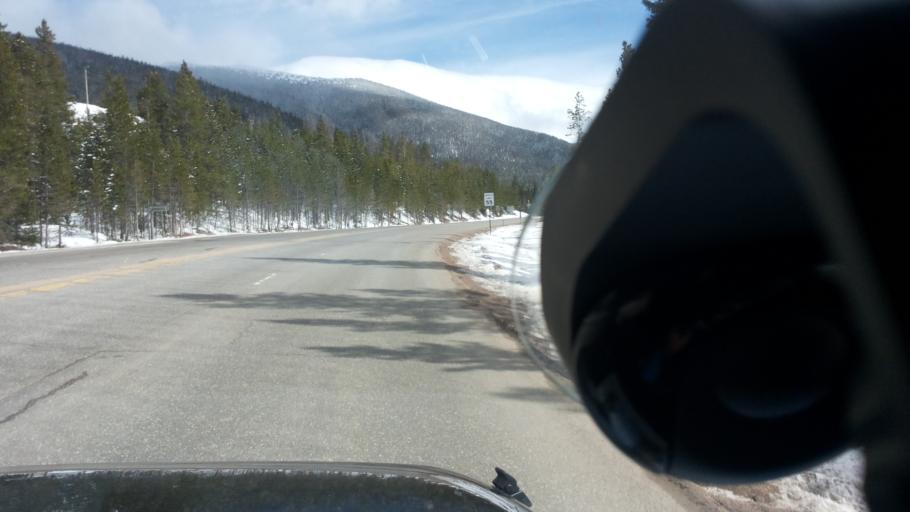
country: US
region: Colorado
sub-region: Grand County
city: Fraser
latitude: 39.8803
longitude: -105.7541
